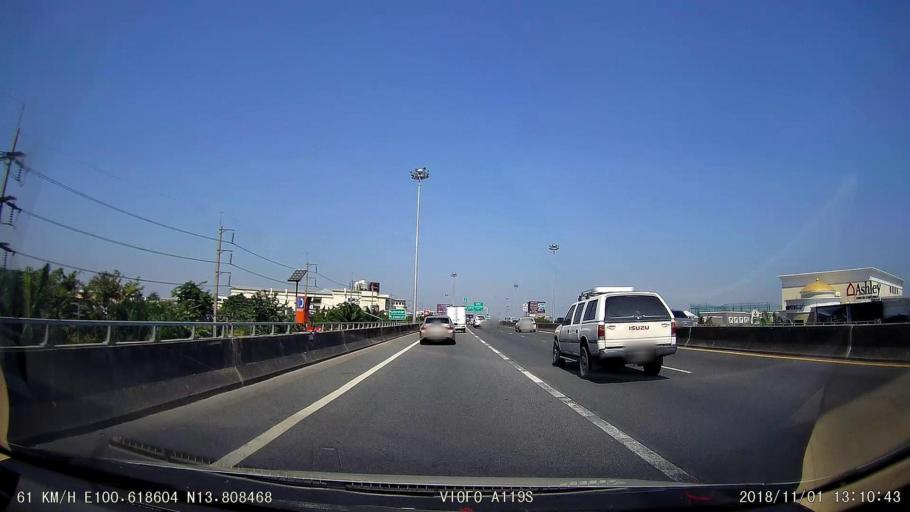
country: TH
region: Bangkok
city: Lat Phrao
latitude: 13.8087
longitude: 100.6187
